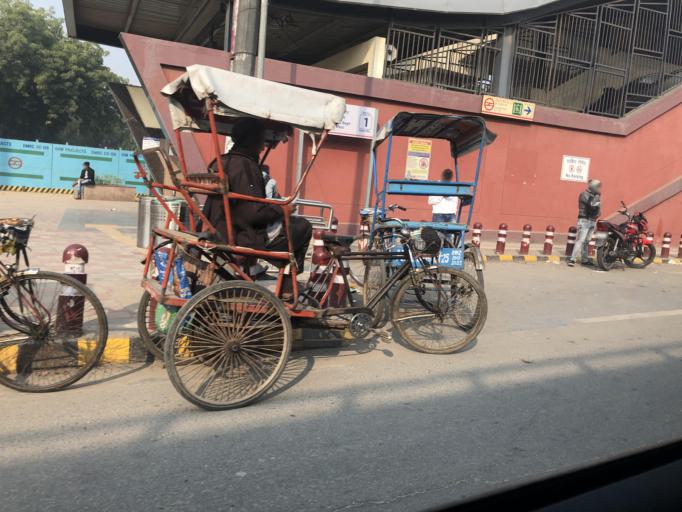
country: IN
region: NCT
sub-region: North West Delhi
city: Pitampura
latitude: 28.6720
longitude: 77.1391
